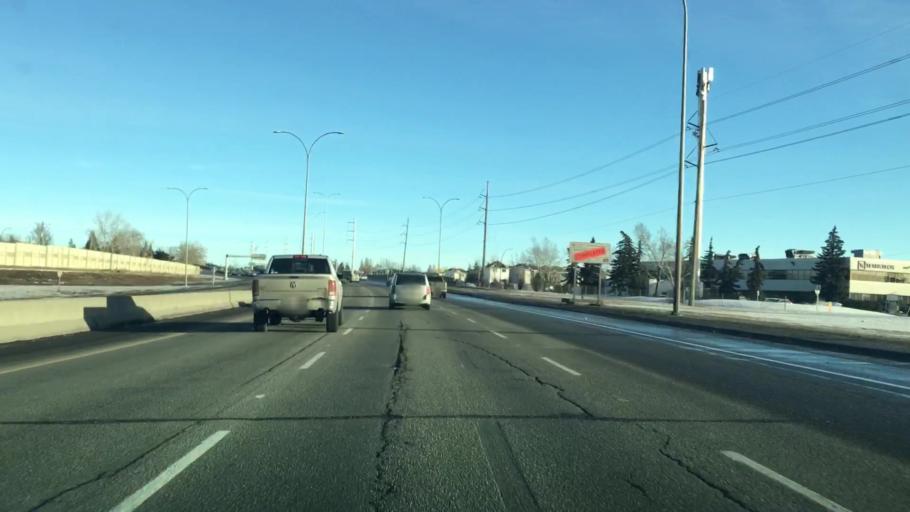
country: CA
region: Alberta
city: Calgary
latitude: 50.9800
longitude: -114.0138
